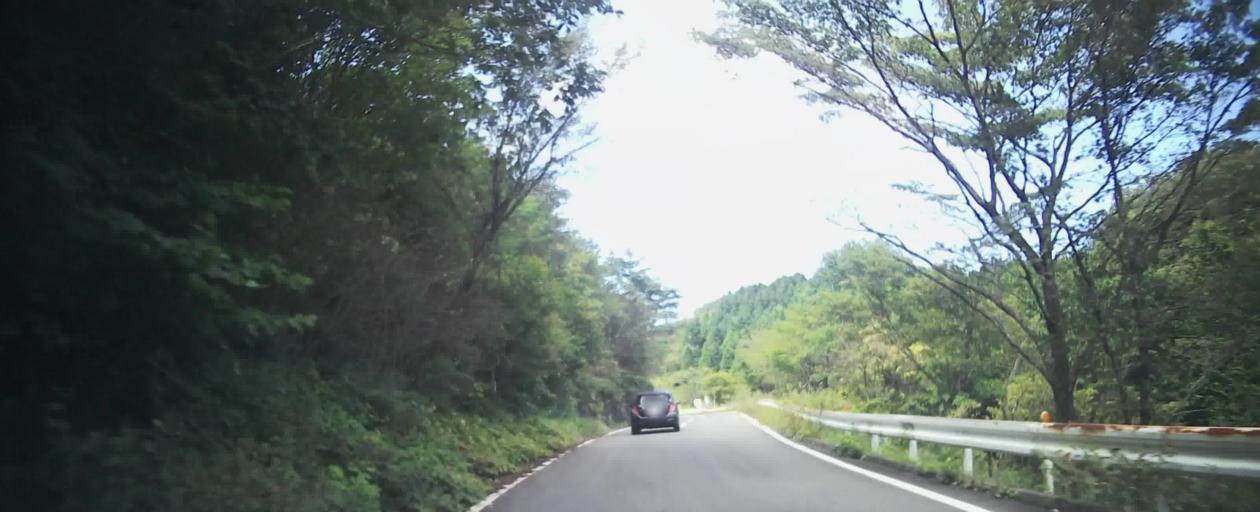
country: JP
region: Gunma
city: Shibukawa
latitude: 36.4674
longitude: 138.8881
